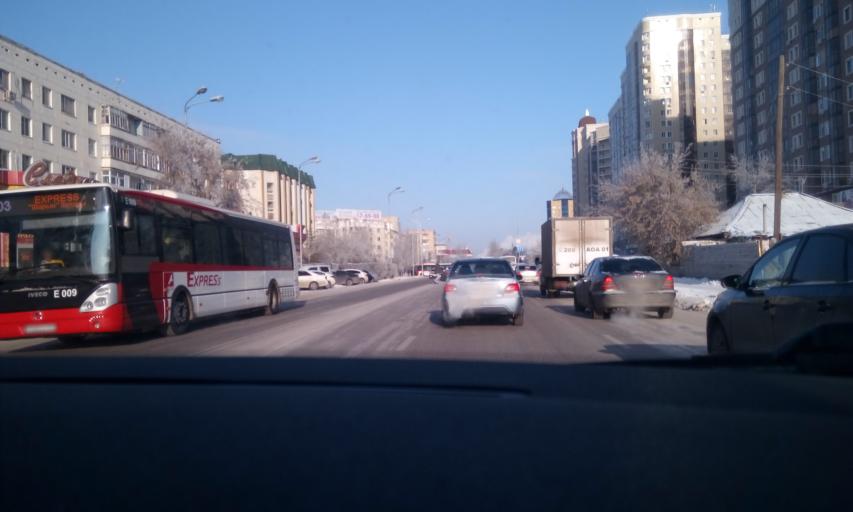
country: KZ
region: Astana Qalasy
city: Astana
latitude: 51.1656
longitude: 71.4404
